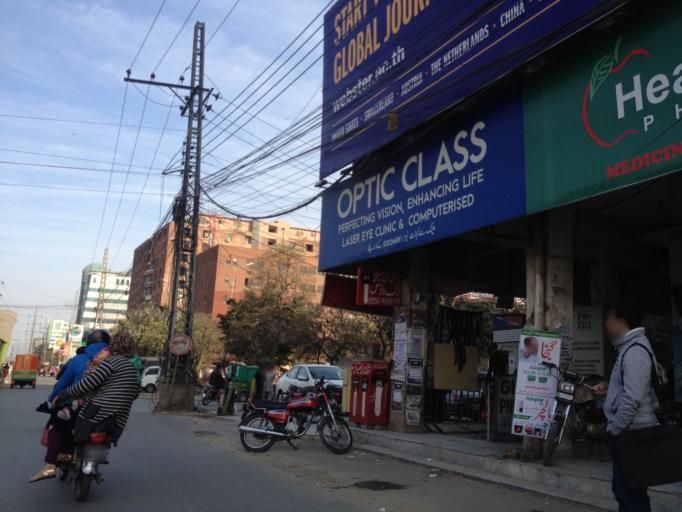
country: PK
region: Punjab
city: Lahore
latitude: 31.5007
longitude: 74.3201
